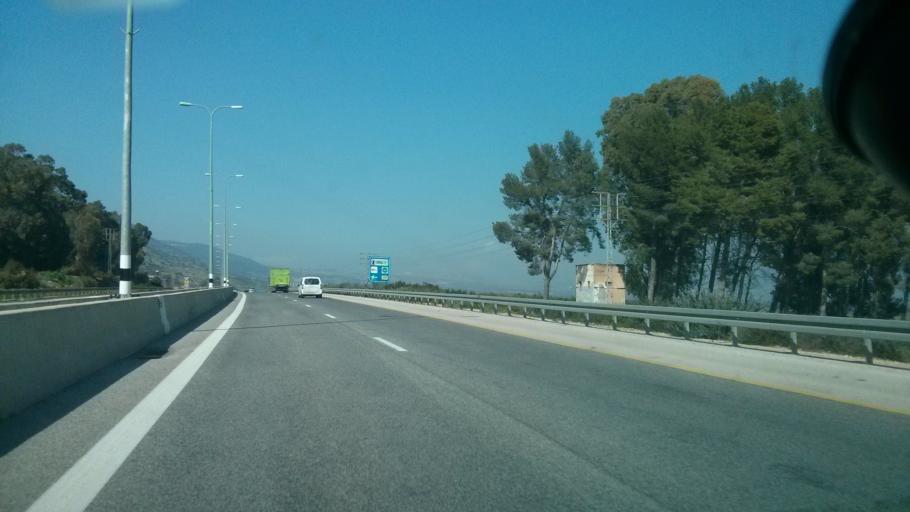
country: IL
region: Northern District
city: Qiryat Shemona
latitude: 33.1188
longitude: 35.5718
